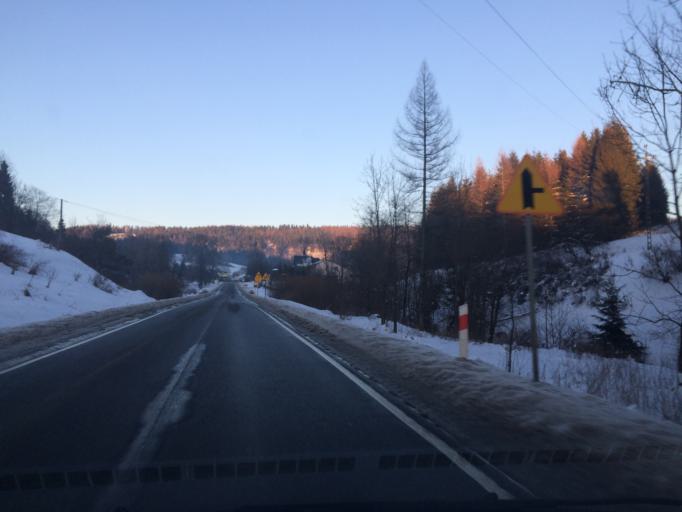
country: PL
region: Subcarpathian Voivodeship
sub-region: Powiat bieszczadzki
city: Czarna
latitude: 49.3441
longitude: 22.6784
